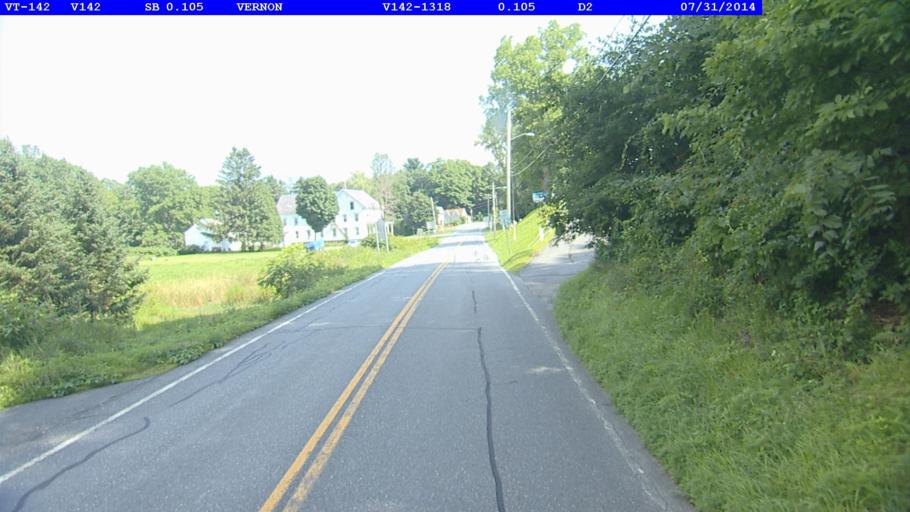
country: US
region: Massachusetts
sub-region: Franklin County
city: Northfield
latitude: 42.7282
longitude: -72.4660
